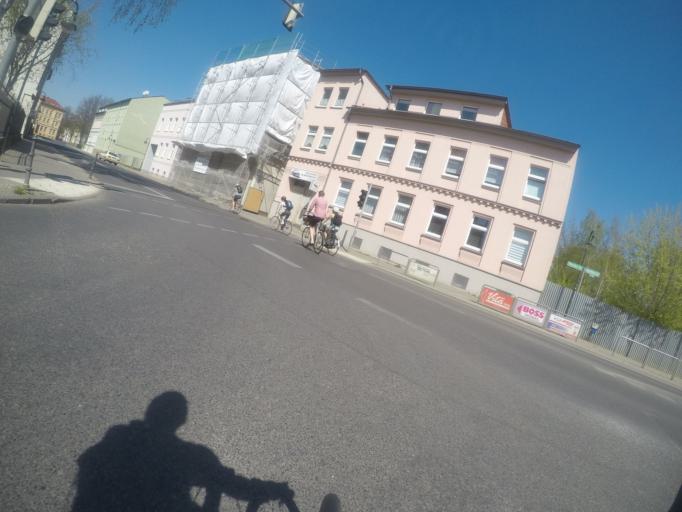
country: DE
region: Brandenburg
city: Bernau bei Berlin
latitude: 52.6781
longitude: 13.5951
